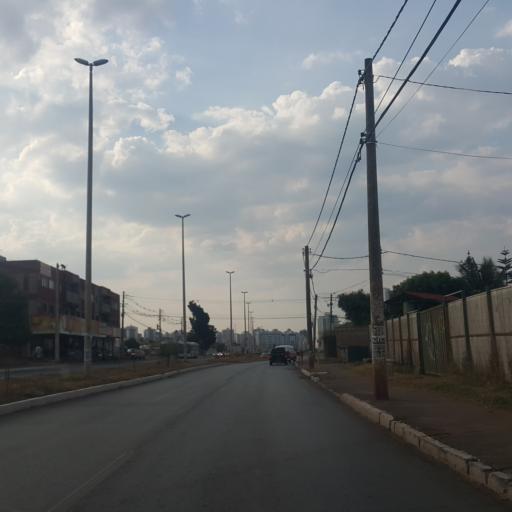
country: BR
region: Federal District
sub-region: Brasilia
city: Brasilia
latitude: -15.8551
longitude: -48.0307
